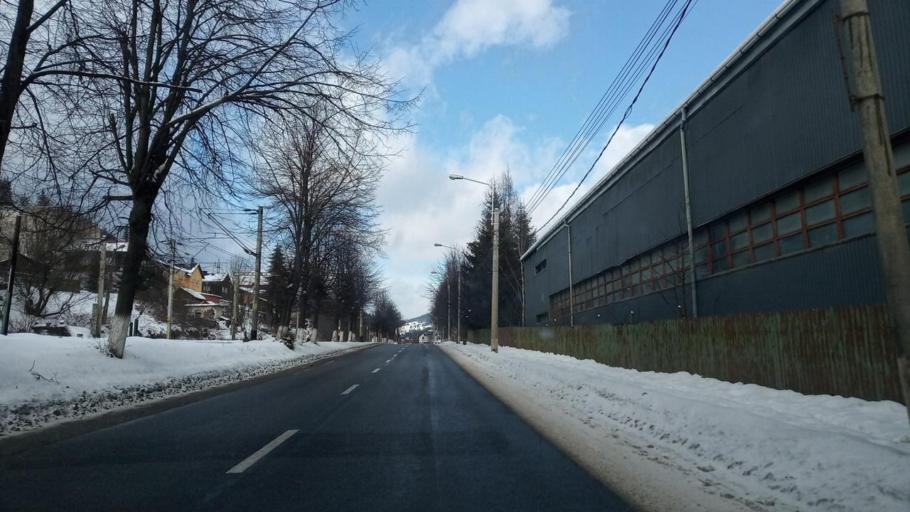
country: RO
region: Suceava
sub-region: Municipiul Vatra Dornei
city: Vatra Dornei
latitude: 47.3569
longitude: 25.3536
